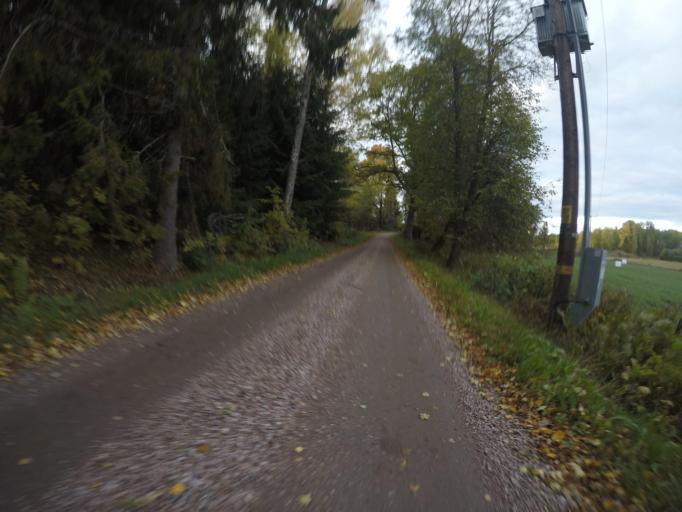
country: SE
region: Vaestmanland
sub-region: Arboga Kommun
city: Tyringe
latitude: 59.2945
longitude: 16.0051
